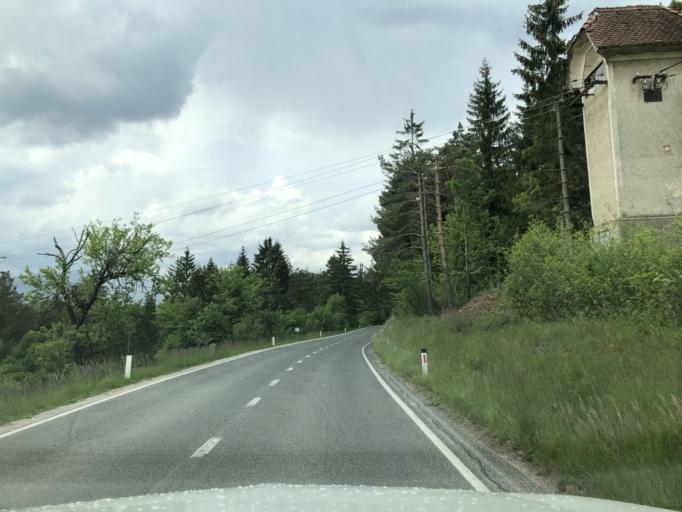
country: SI
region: Bloke
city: Nova Vas
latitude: 45.7601
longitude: 14.4639
